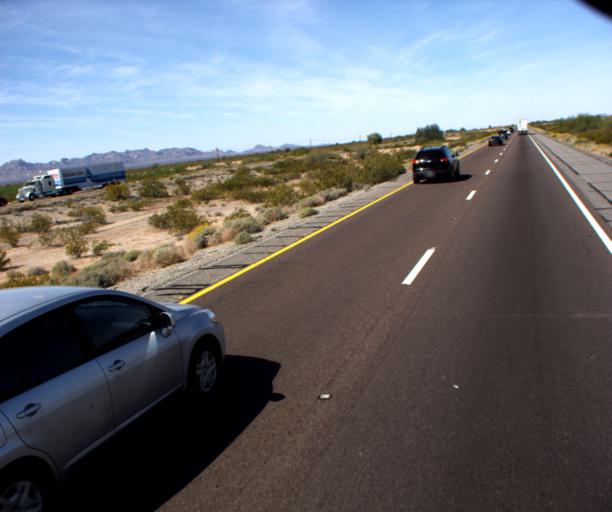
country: US
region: Arizona
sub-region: La Paz County
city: Salome
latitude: 33.5560
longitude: -113.2651
